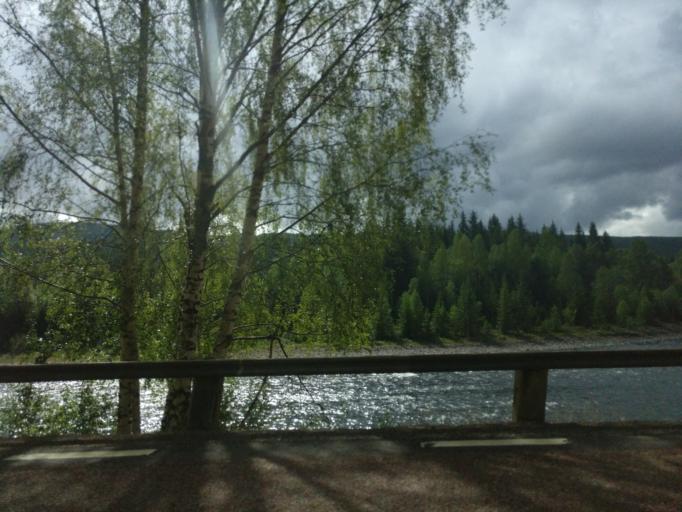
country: SE
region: Vaermland
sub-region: Torsby Kommun
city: Torsby
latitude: 60.7499
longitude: 12.8088
